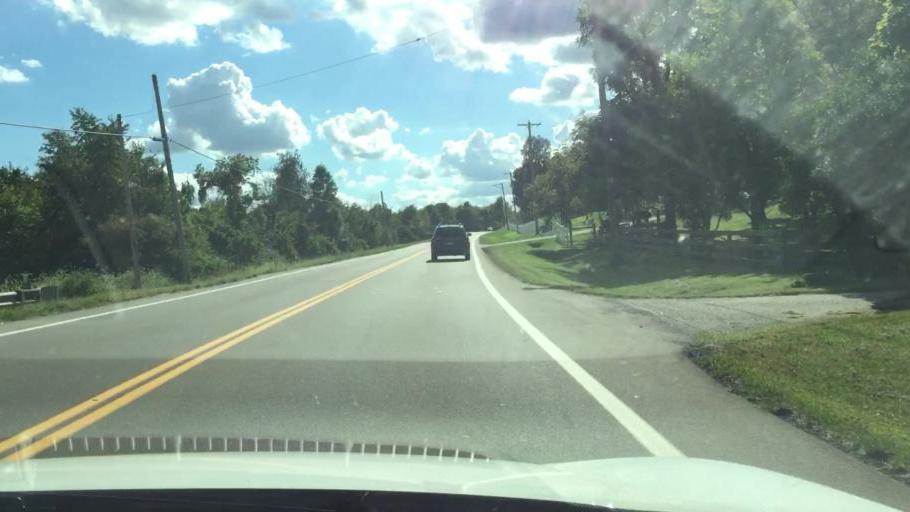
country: US
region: Ohio
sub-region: Clark County
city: Northridge
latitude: 39.9835
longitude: -83.7350
